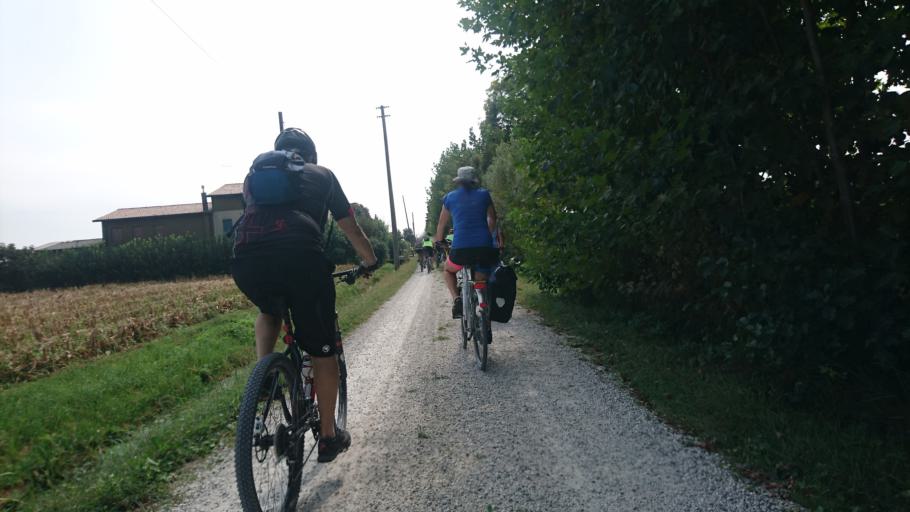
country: IT
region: Veneto
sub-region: Provincia di Padova
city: San Giorgio in Bosco
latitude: 45.5853
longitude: 11.7704
